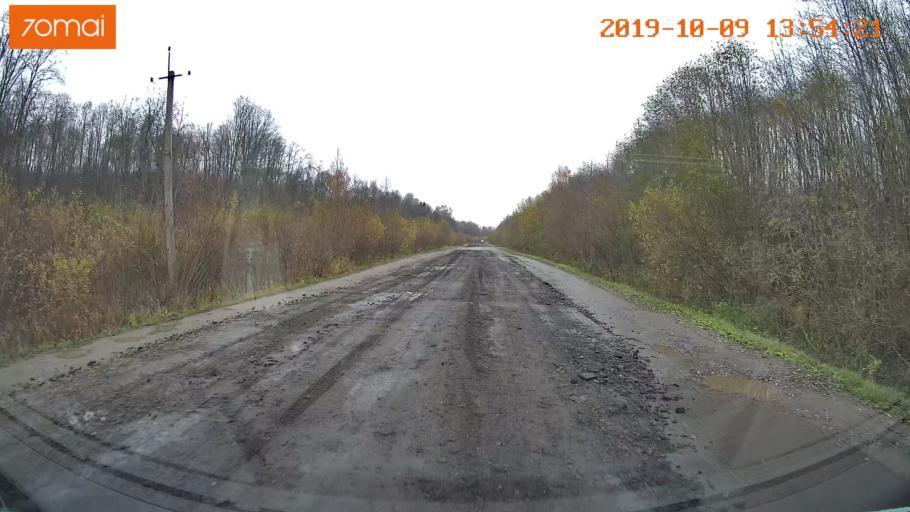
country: RU
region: Kostroma
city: Buy
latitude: 58.4204
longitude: 41.2665
